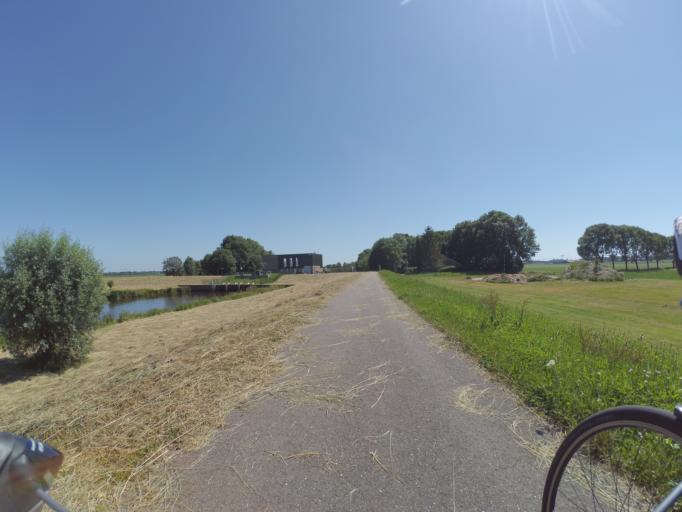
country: NL
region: North Brabant
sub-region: Gemeente Waalwijk
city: Waspik
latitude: 51.7127
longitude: 4.9044
